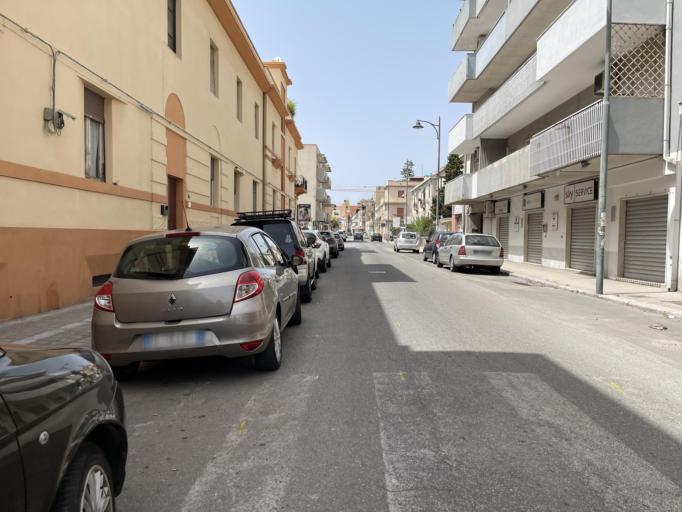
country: IT
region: Calabria
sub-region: Provincia di Reggio Calabria
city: Reggio Calabria
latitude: 38.0980
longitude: 15.6431
